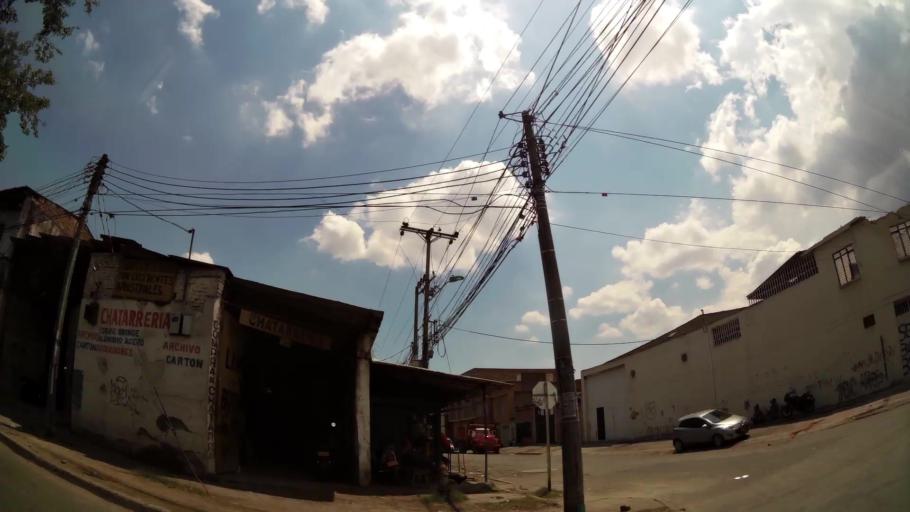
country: CO
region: Valle del Cauca
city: Cali
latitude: 3.4538
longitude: -76.5094
